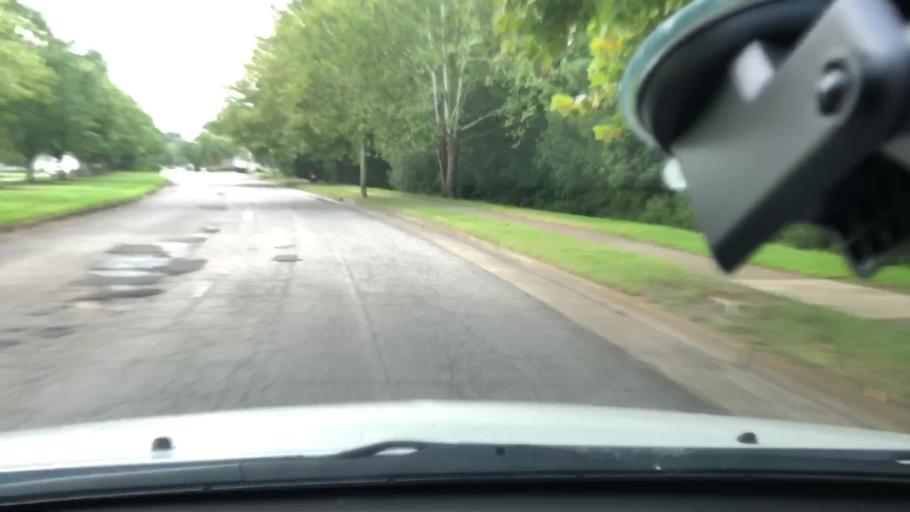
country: US
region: Virginia
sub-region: City of Chesapeake
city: Chesapeake
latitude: 36.7158
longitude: -76.2889
